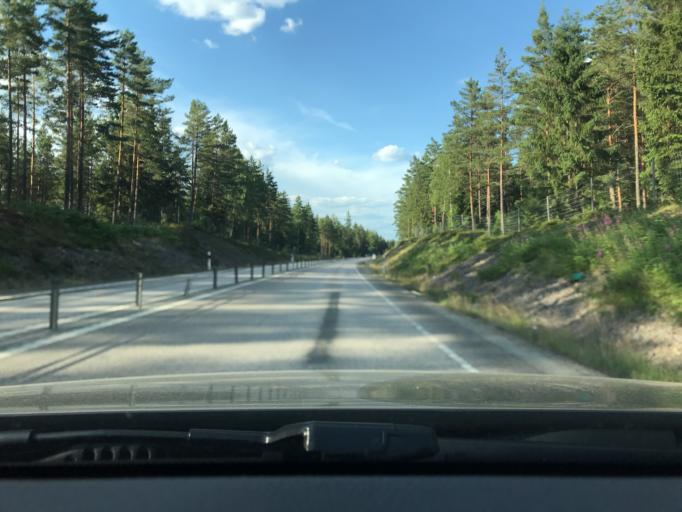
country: SE
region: Kronoberg
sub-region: Vaxjo Kommun
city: Braas
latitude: 57.0258
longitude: 15.0601
